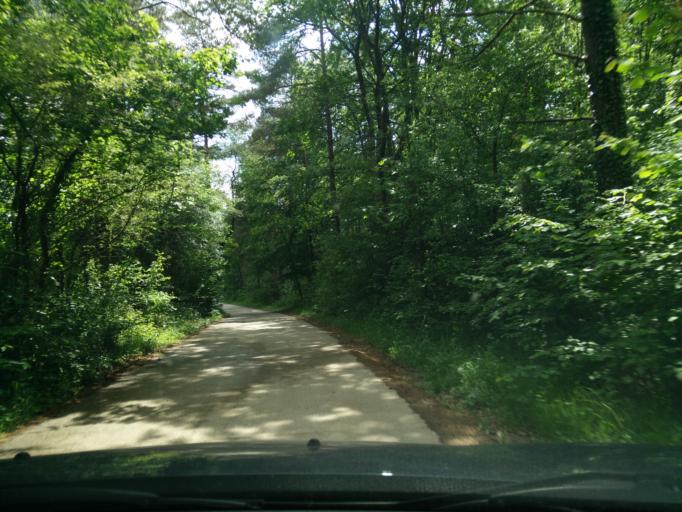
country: FR
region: Champagne-Ardenne
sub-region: Departement des Ardennes
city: Vireux-Molhain
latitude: 50.0824
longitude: 4.6175
